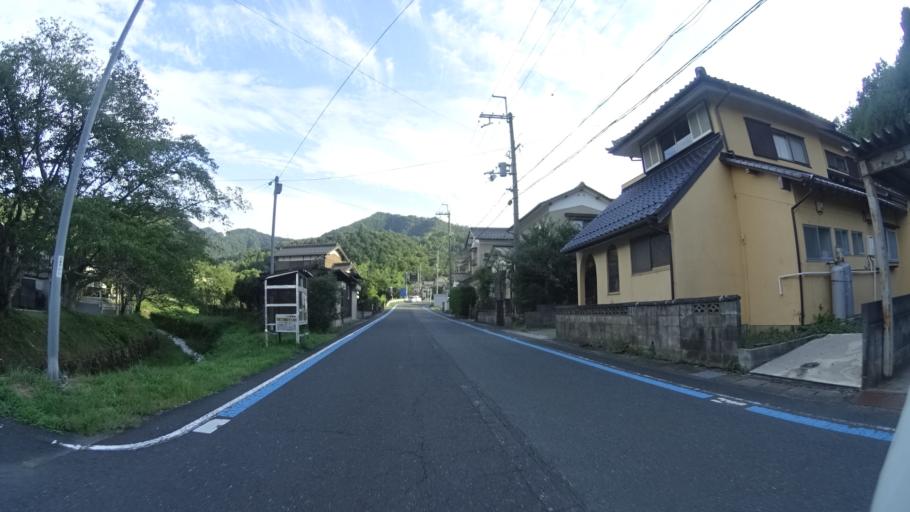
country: JP
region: Kyoto
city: Maizuru
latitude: 35.4490
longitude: 135.3973
